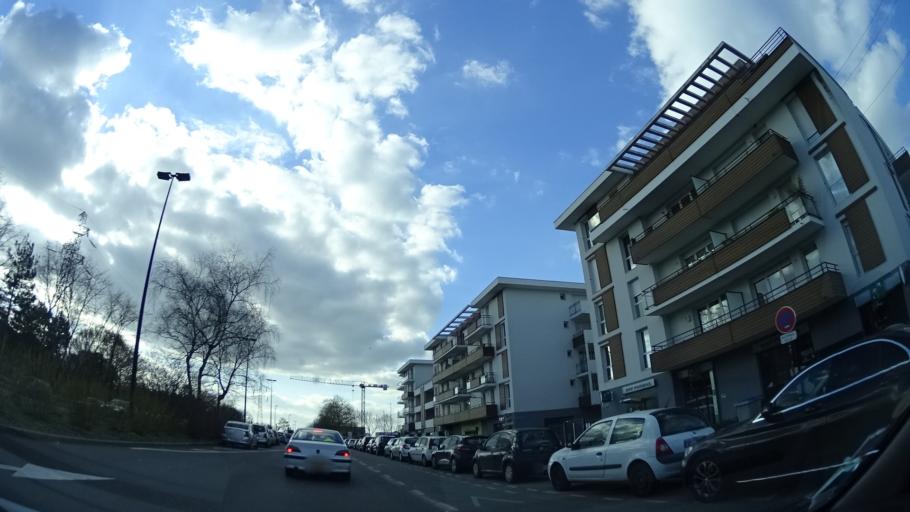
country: FR
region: Pays de la Loire
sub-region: Departement de la Loire-Atlantique
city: Sainte-Luce-sur-Loire
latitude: 47.2585
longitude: -1.5180
